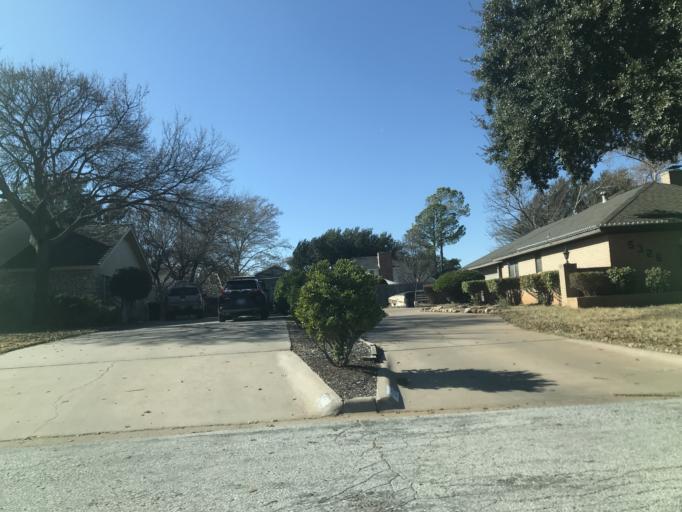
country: US
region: Texas
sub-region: Taylor County
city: Abilene
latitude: 32.3823
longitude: -99.7588
